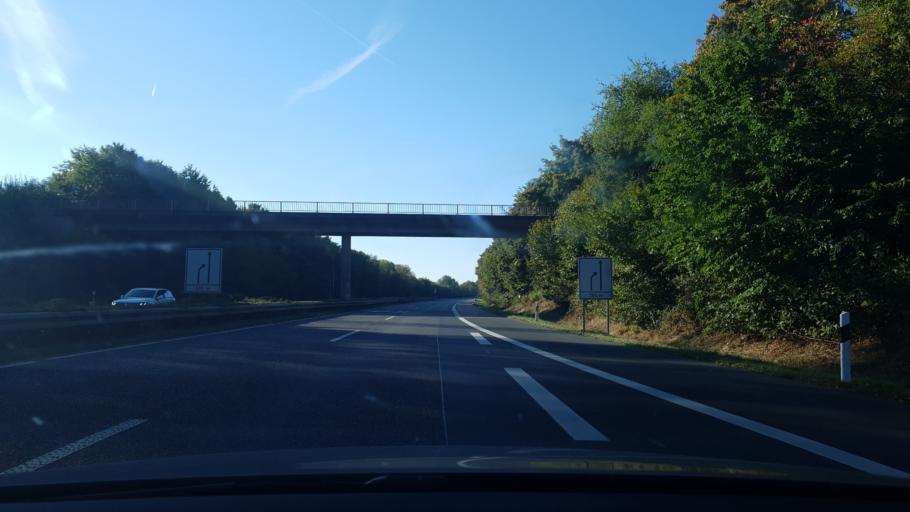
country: DE
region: Hesse
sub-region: Regierungsbezirk Giessen
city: Langgons
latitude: 50.4890
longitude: 8.6558
